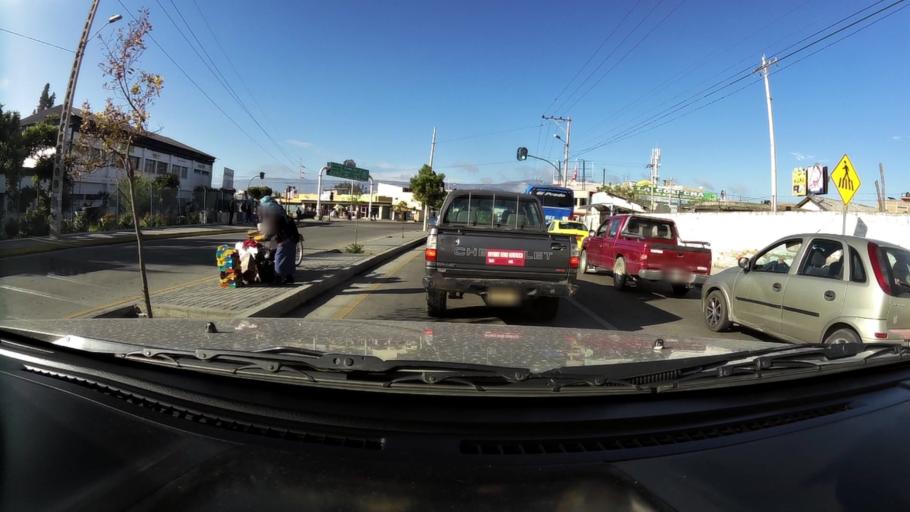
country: EC
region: Chimborazo
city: Riobamba
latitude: -1.6890
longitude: -78.6316
